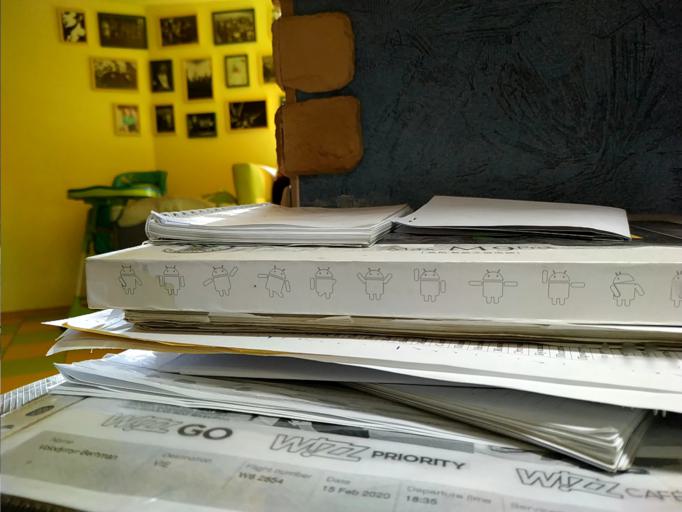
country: RU
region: Pskov
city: Plyussa
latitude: 58.4882
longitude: 29.5704
